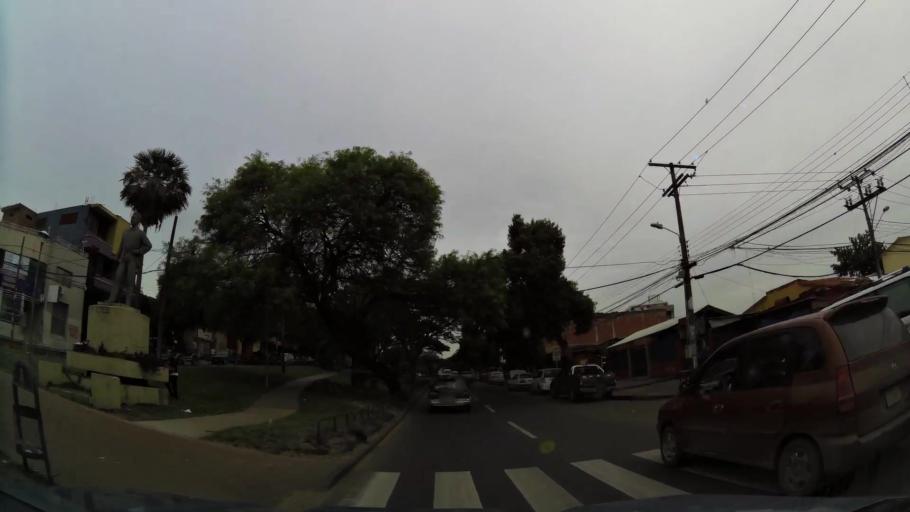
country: BO
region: Santa Cruz
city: Santa Cruz de la Sierra
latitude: -17.7956
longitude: -63.1867
